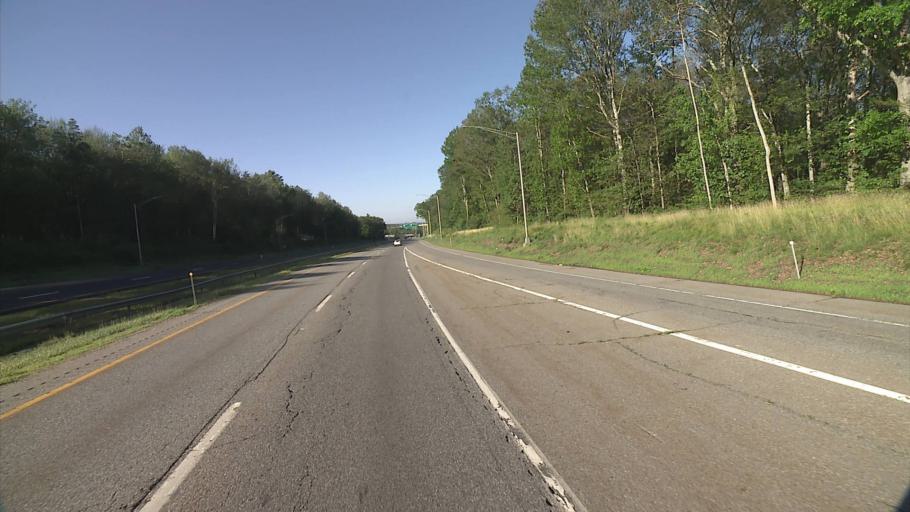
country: US
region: Connecticut
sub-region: Windham County
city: Danielson
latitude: 41.8003
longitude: -71.8734
